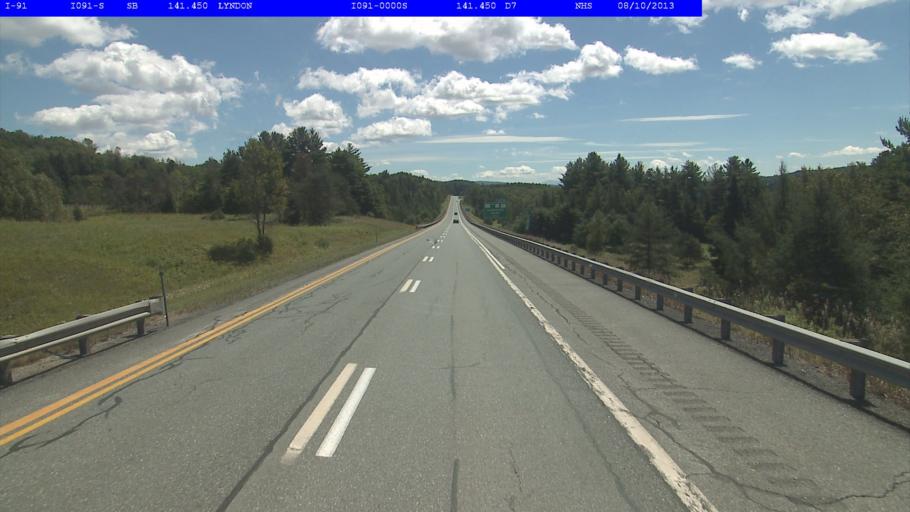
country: US
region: Vermont
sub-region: Caledonia County
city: Lyndonville
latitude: 44.5715
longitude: -72.0417
